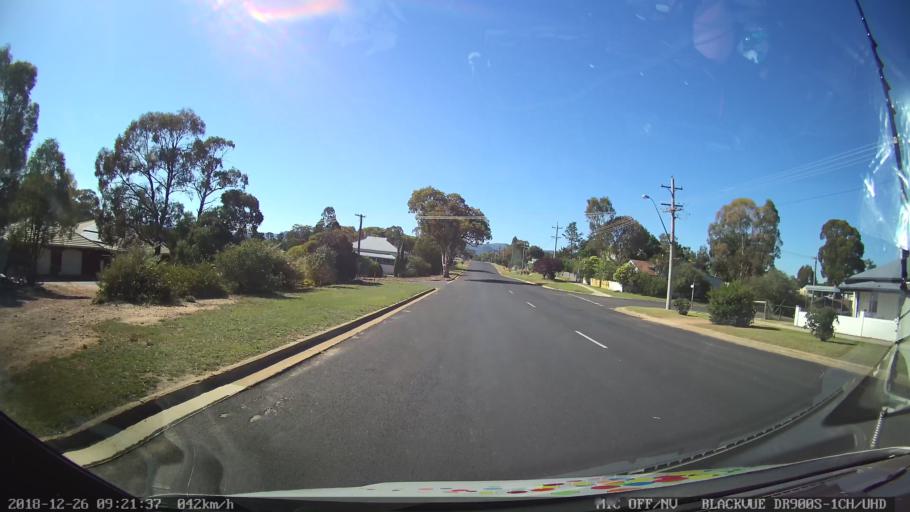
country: AU
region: New South Wales
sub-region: Mid-Western Regional
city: Kandos
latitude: -32.8014
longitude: 149.9737
